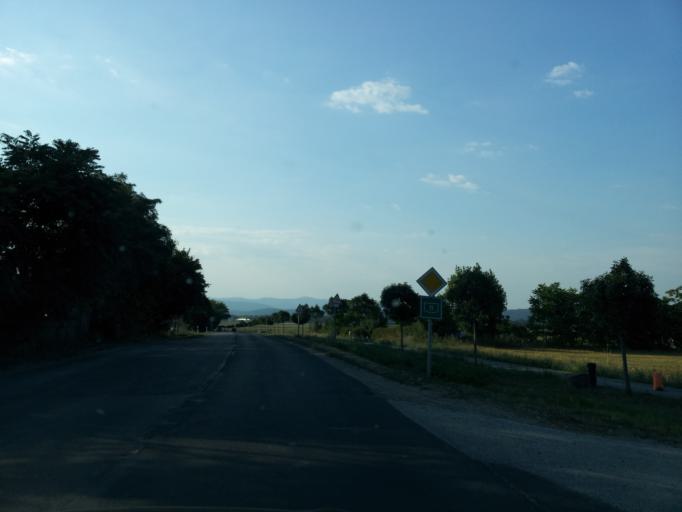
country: HU
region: Pest
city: Dunabogdany
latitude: 47.7719
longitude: 19.0590
